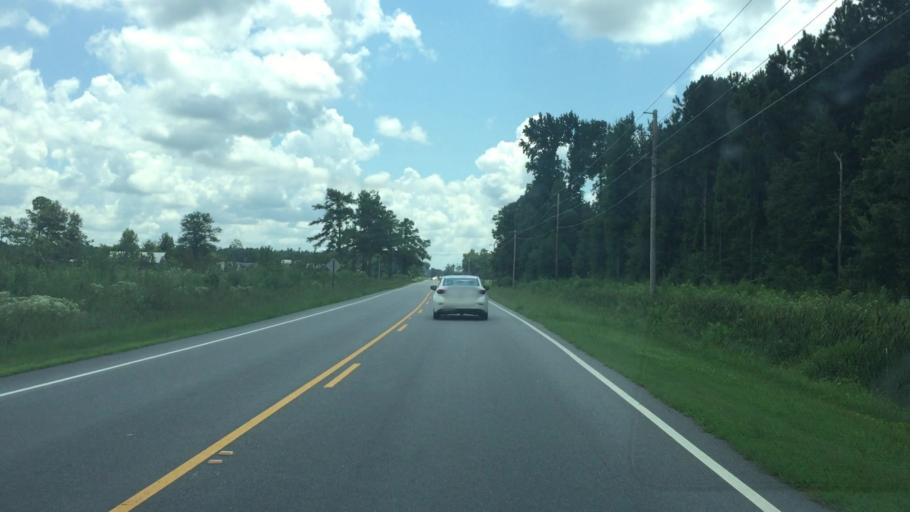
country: US
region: North Carolina
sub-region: Columbus County
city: Chadbourn
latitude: 34.2317
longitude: -78.8244
